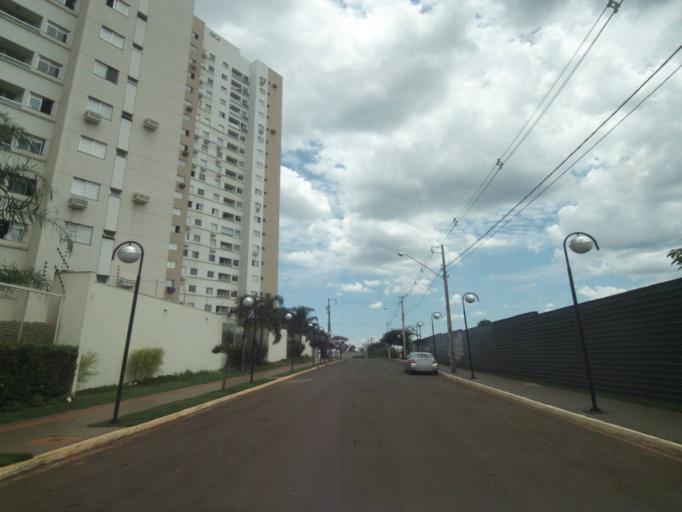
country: BR
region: Parana
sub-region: Londrina
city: Londrina
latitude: -23.3335
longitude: -51.1834
